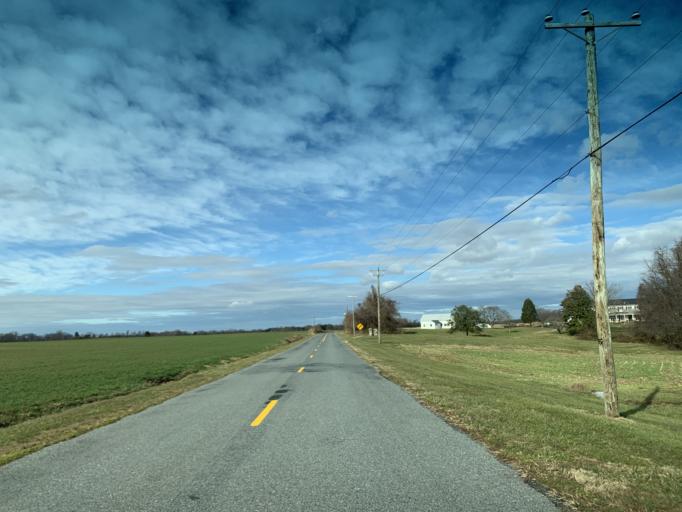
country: US
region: Maryland
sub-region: Kent County
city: Chestertown
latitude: 39.3422
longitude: -76.0512
